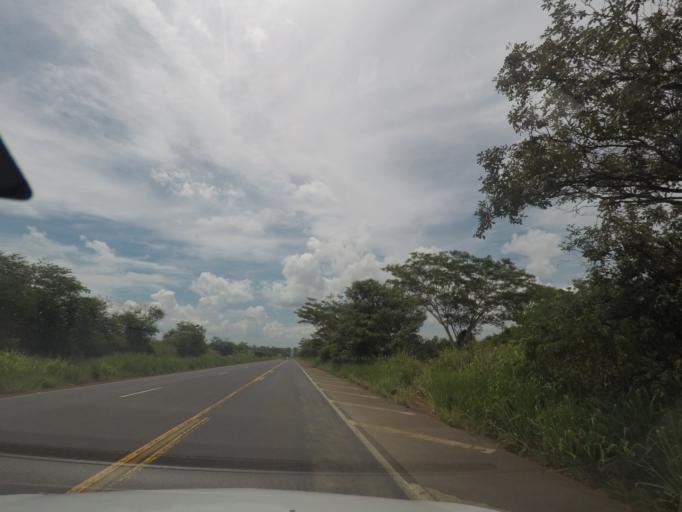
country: BR
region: Sao Paulo
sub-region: Barretos
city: Barretos
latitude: -20.4165
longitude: -48.6319
